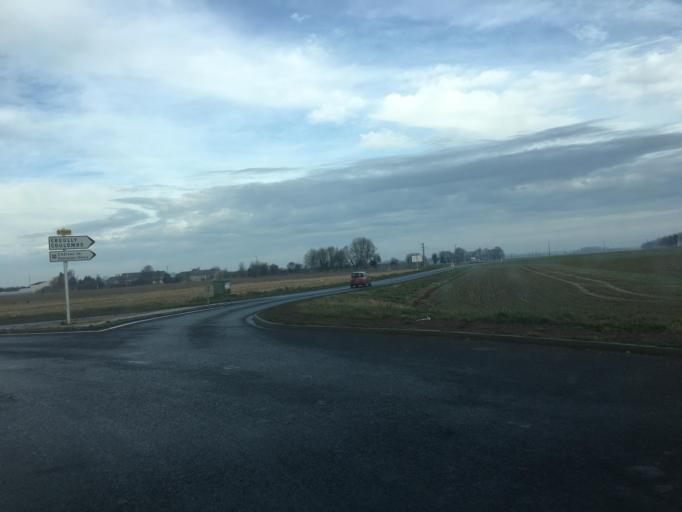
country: FR
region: Lower Normandy
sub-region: Departement du Calvados
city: Creully
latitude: 49.2350
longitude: -0.5778
